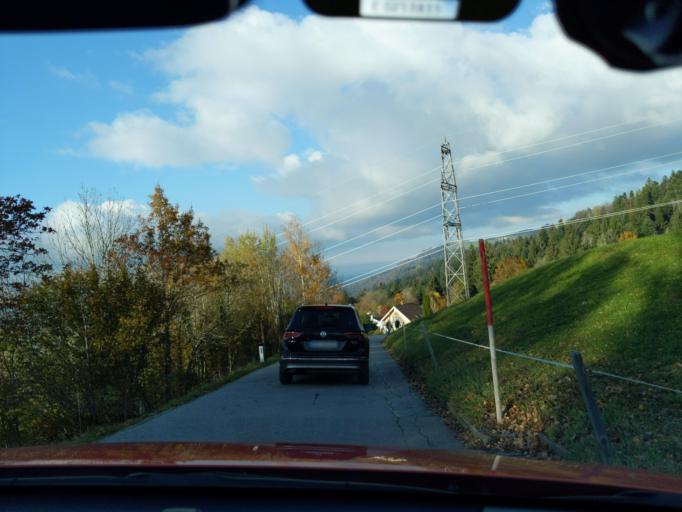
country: AT
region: Vorarlberg
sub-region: Politischer Bezirk Bregenz
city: Bregenz
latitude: 47.5160
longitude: 9.7629
